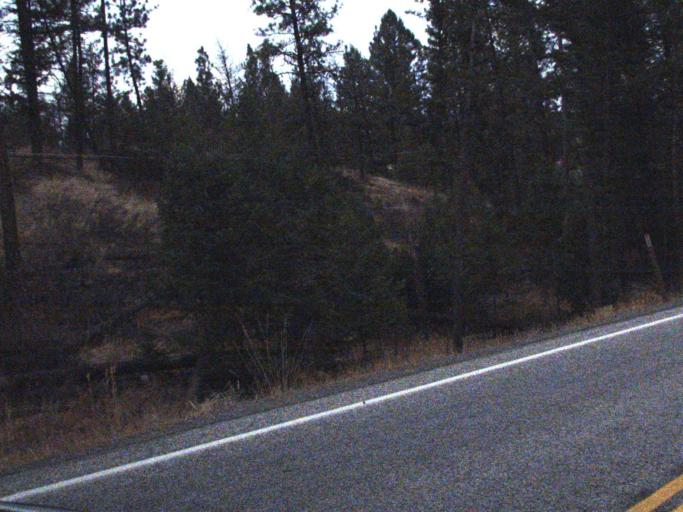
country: US
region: Washington
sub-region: Ferry County
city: Republic
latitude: 48.6472
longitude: -118.6853
